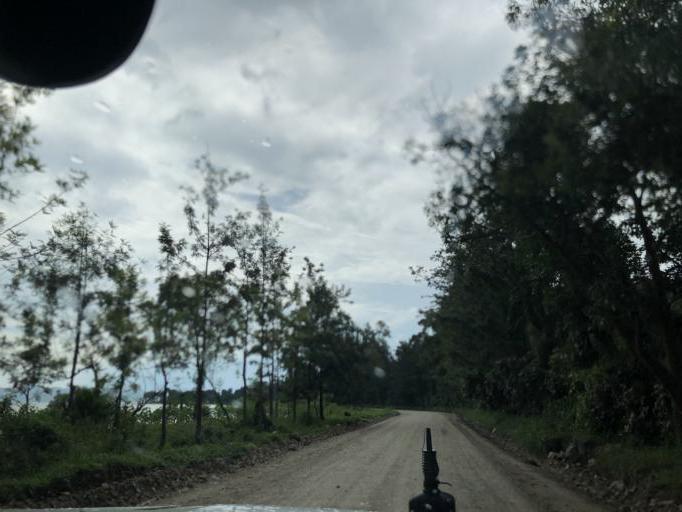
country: CD
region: Nord Kivu
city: Sake
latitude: -1.5985
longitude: 29.0380
